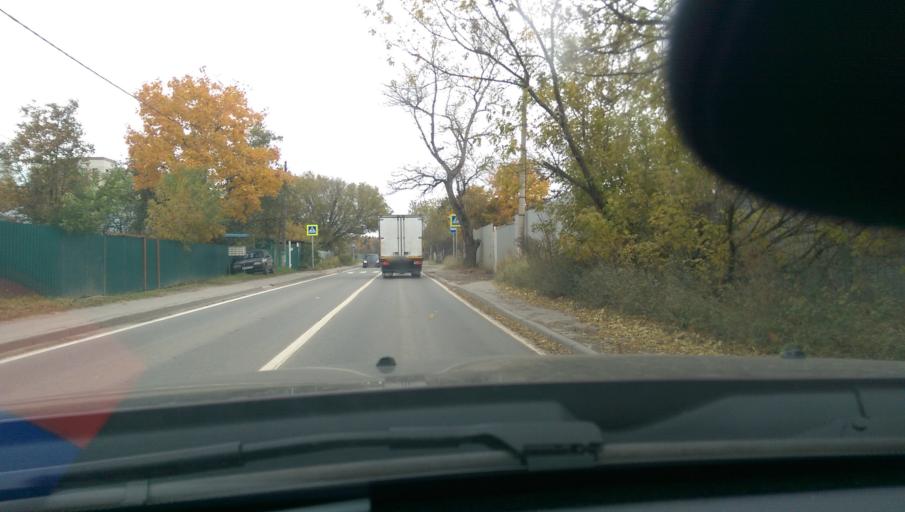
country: RU
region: Moskovskaya
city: Pirogovskiy
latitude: 55.9845
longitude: 37.7271
